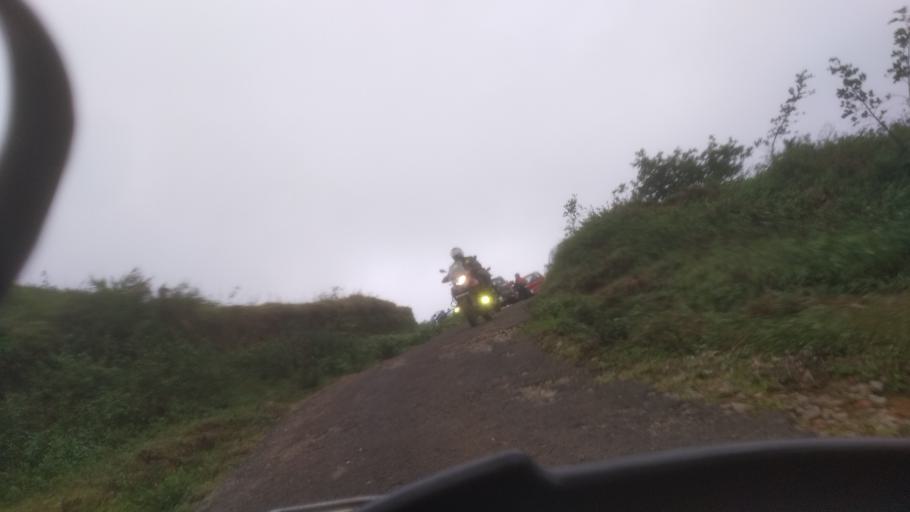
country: IN
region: Tamil Nadu
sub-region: Theni
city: Kombai
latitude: 9.8870
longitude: 77.2215
